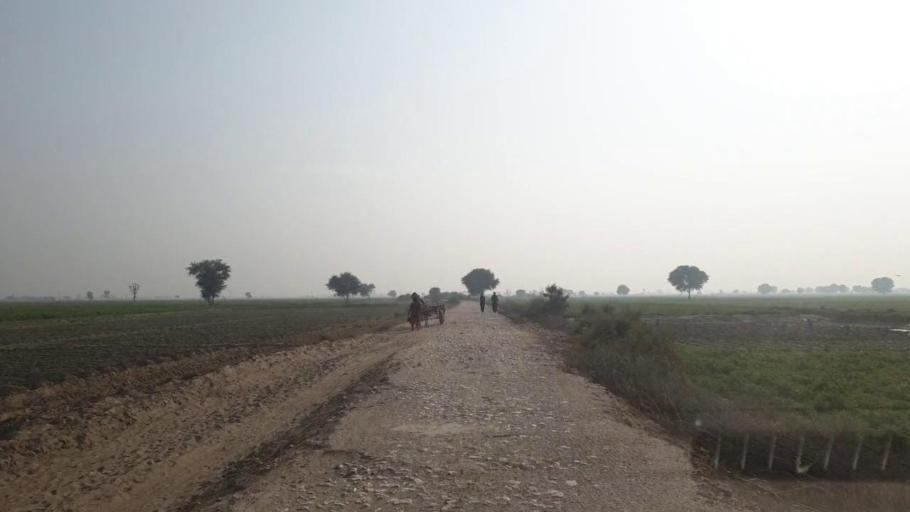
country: PK
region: Sindh
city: Hala
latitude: 25.7677
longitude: 68.3872
